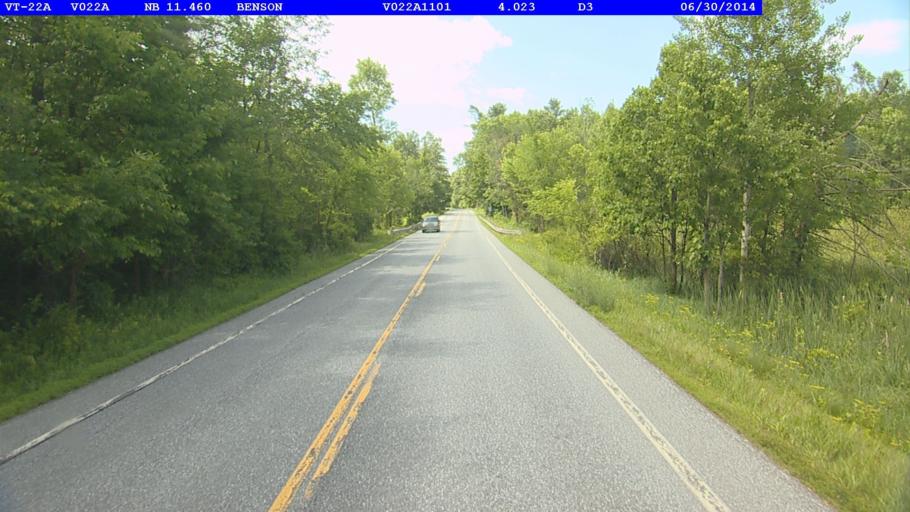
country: US
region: Vermont
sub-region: Rutland County
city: Fair Haven
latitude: 43.7260
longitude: -73.3015
